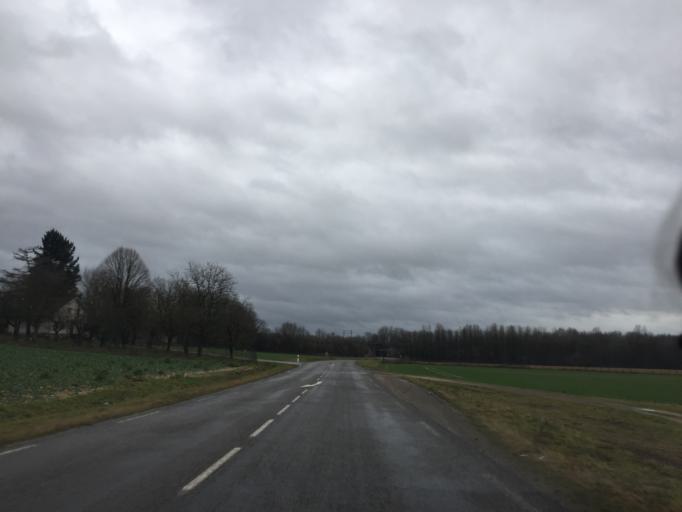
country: FR
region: Franche-Comte
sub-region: Departement du Jura
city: Dole
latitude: 47.1424
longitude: 5.5648
